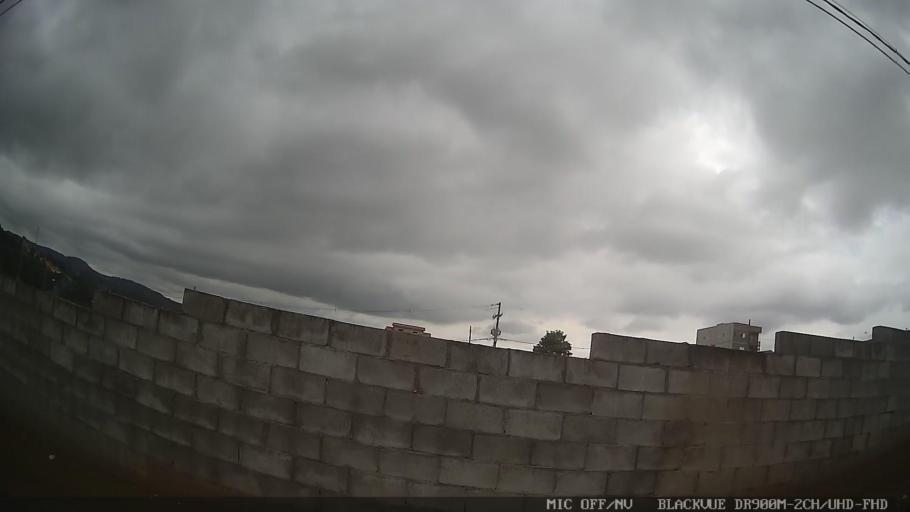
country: BR
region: Sao Paulo
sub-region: Atibaia
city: Atibaia
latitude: -23.1253
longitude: -46.5913
